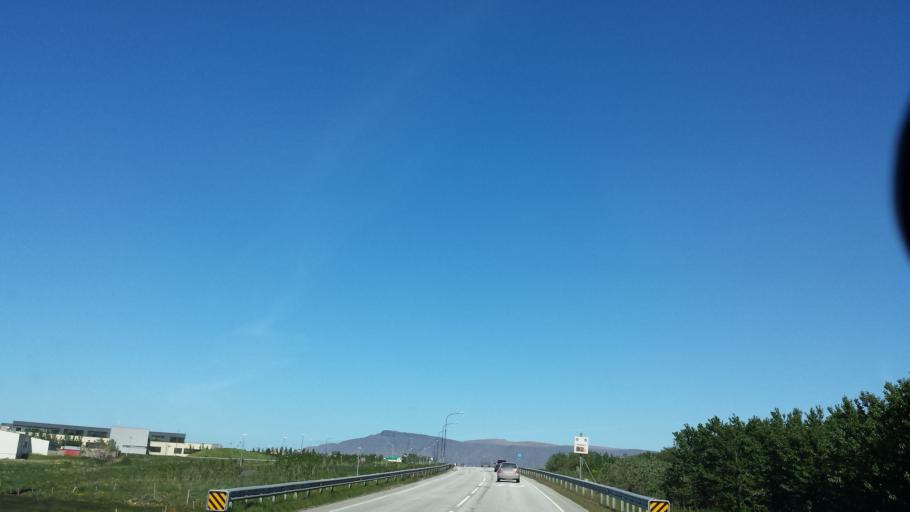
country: IS
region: Capital Region
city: Reykjavik
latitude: 64.2356
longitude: -21.8204
